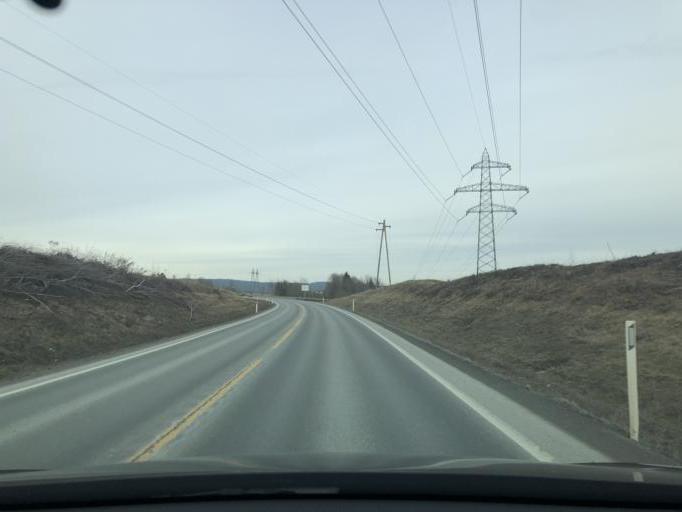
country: NO
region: Buskerud
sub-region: Ringerike
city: Honefoss
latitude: 60.1797
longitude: 10.2308
